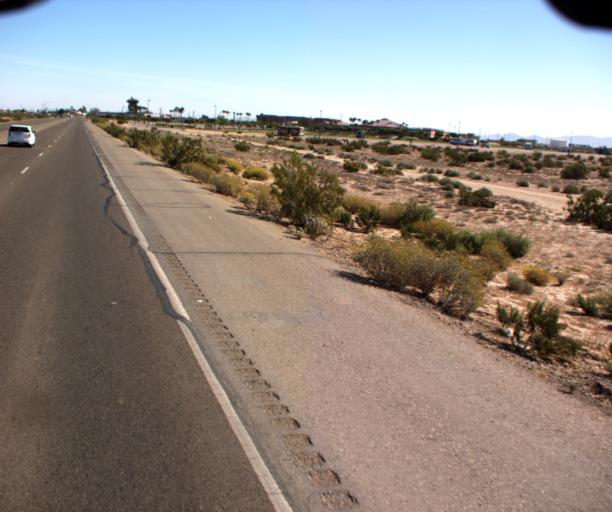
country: US
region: Arizona
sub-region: Yuma County
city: Somerton
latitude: 32.6051
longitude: -114.6572
